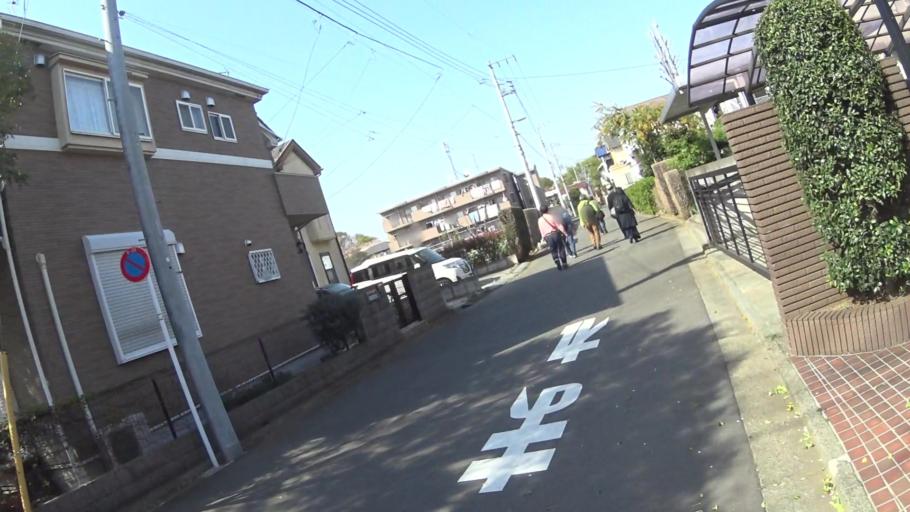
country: JP
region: Tokyo
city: Kokubunji
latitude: 35.7130
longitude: 139.4907
